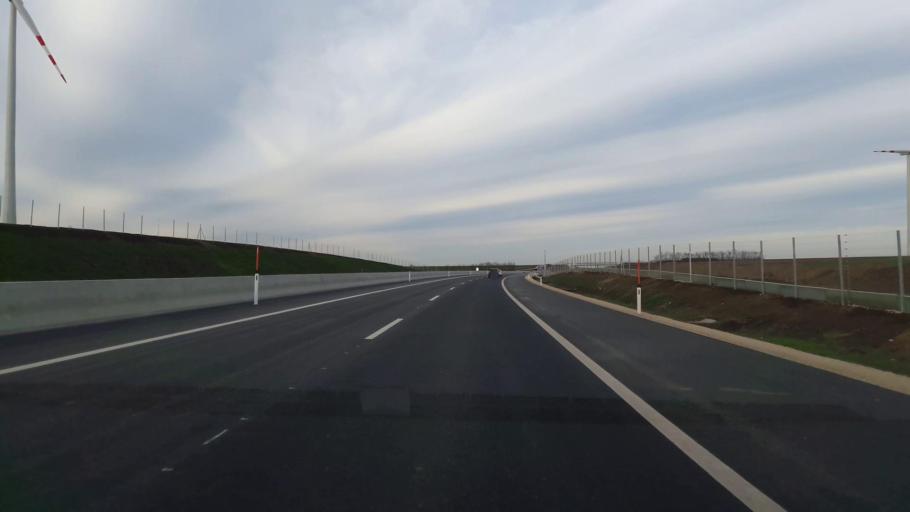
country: AT
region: Lower Austria
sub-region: Politischer Bezirk Mistelbach
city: Grosskrut
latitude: 48.6226
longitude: 16.6761
